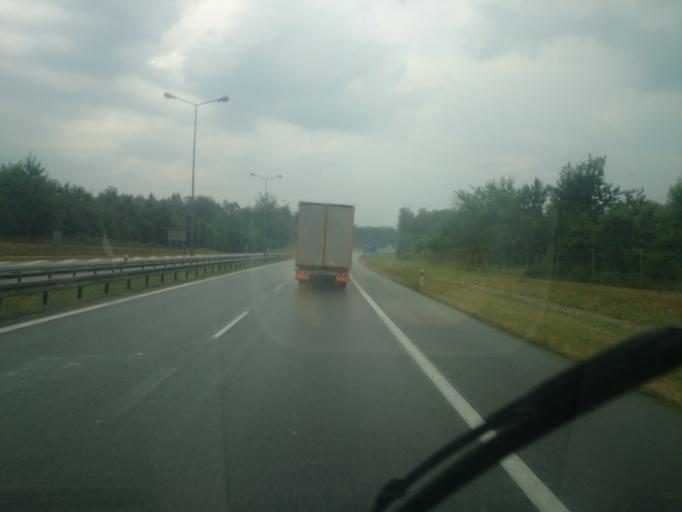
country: PL
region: Opole Voivodeship
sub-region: Powiat strzelecki
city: Ujazd
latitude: 50.4442
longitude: 18.3534
